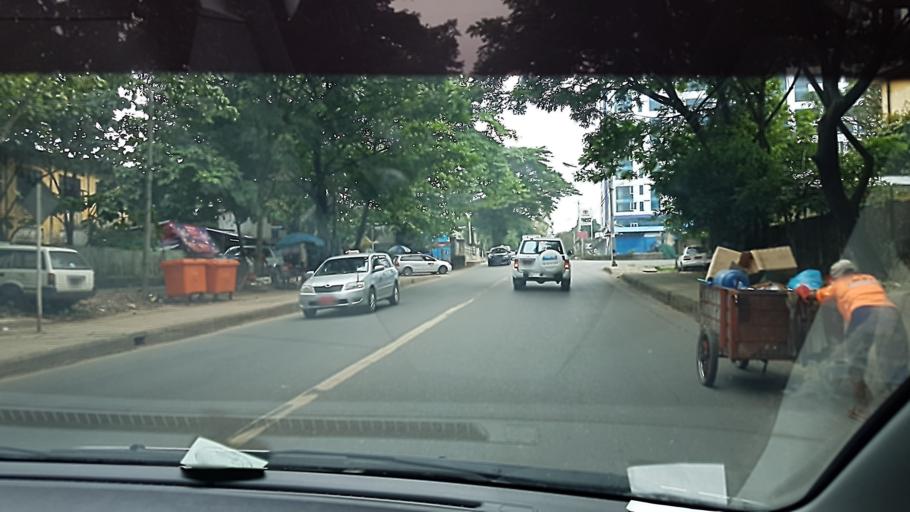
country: MM
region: Yangon
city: Yangon
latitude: 16.7901
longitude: 96.1305
